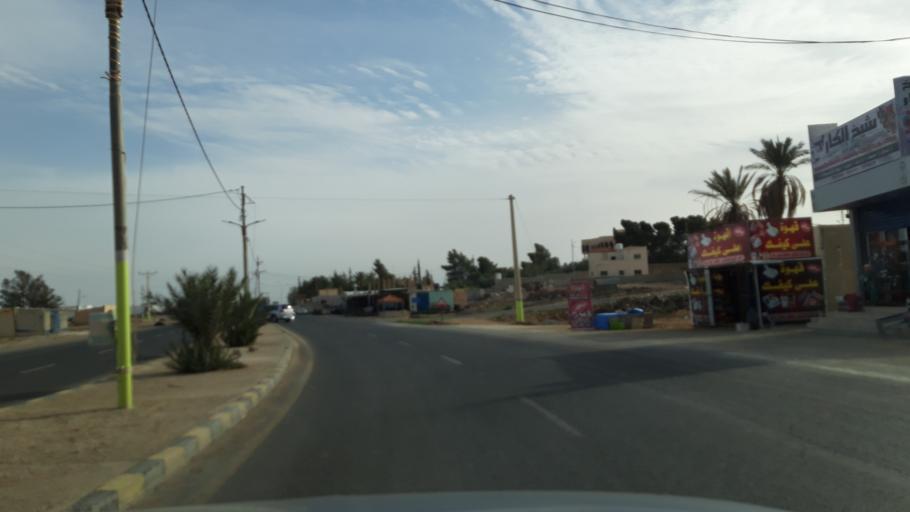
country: JO
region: Amman
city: Al Azraq ash Shamali
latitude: 31.8778
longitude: 36.8253
